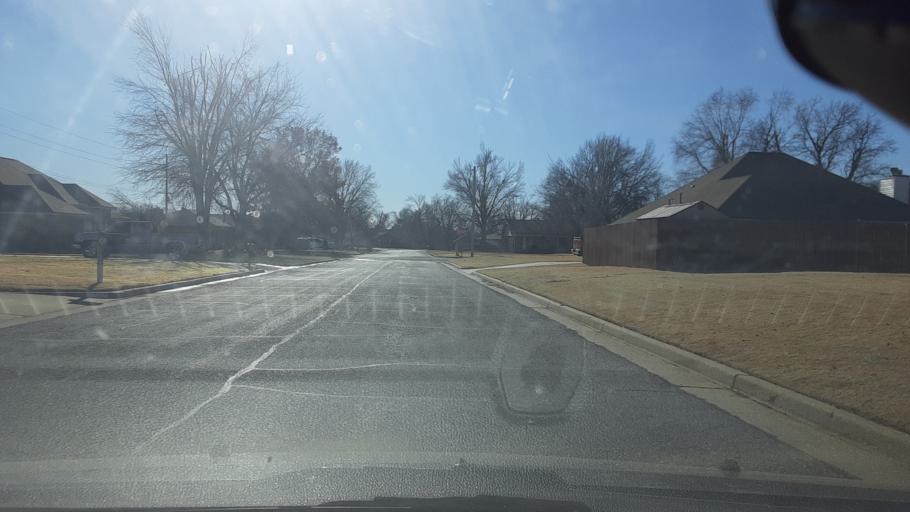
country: US
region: Oklahoma
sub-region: Kay County
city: Ponca City
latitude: 36.7308
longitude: -97.0859
